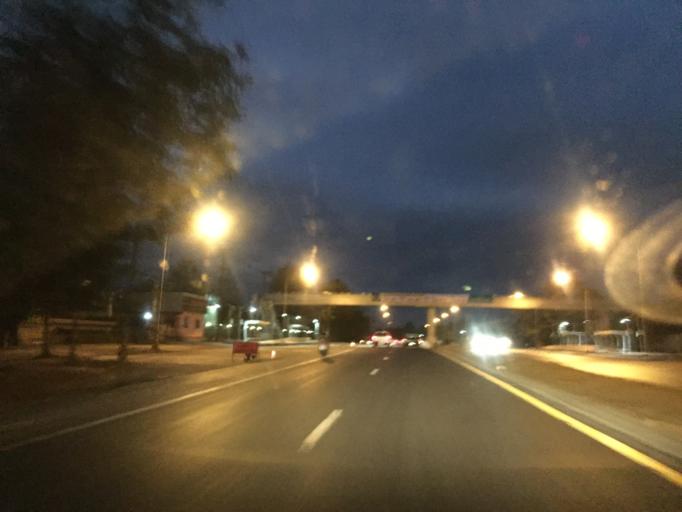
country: TH
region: Changwat Nong Bua Lamphu
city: Na Klang
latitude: 17.2972
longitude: 102.2112
